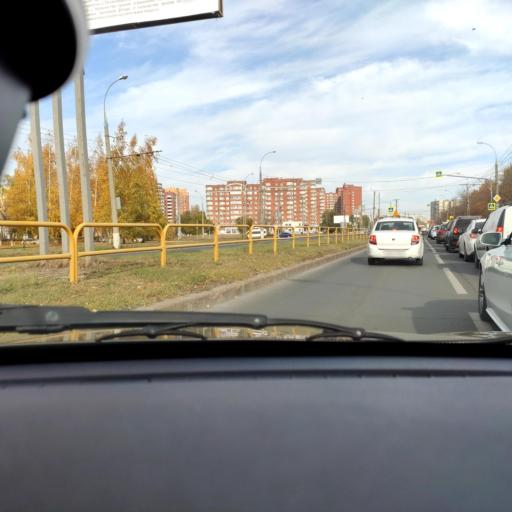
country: RU
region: Samara
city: Tol'yatti
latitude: 53.5113
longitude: 49.3053
